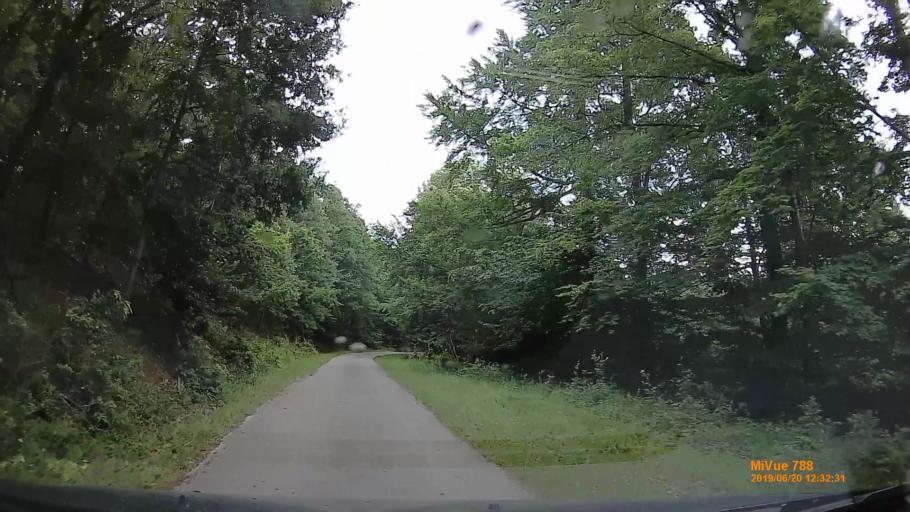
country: HU
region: Baranya
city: Hosszuheteny
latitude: 46.1953
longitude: 18.3606
